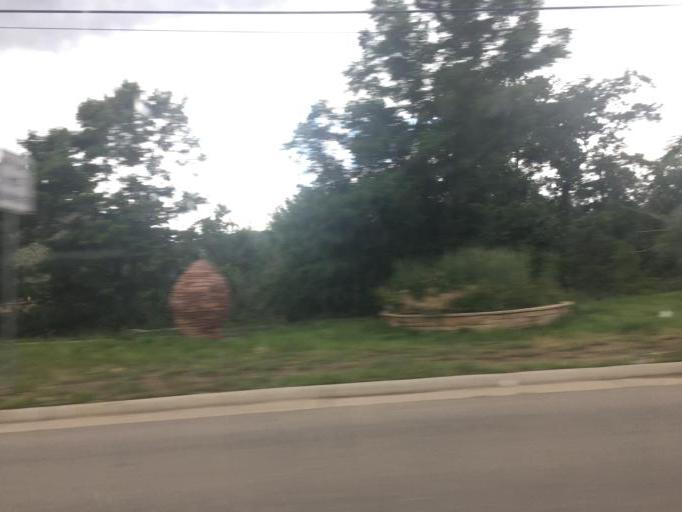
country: US
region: Colorado
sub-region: Boulder County
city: Lyons
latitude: 40.2183
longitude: -105.2601
